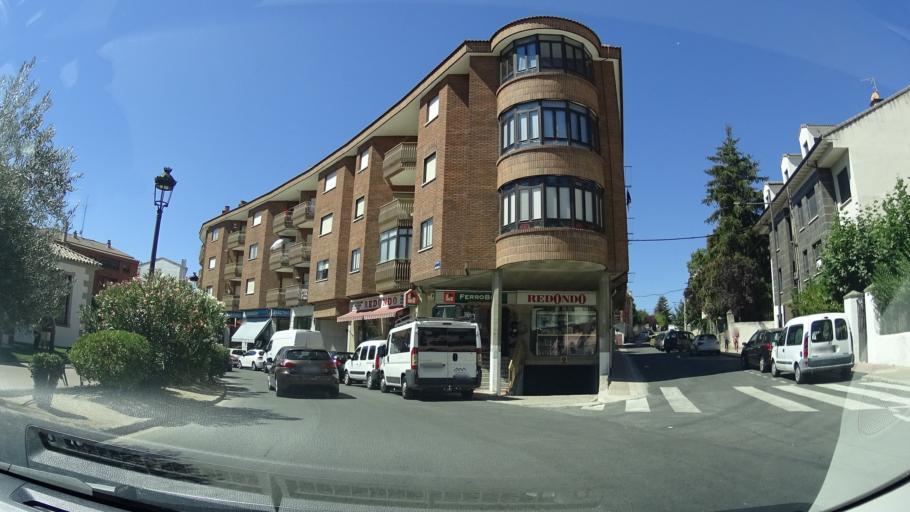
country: ES
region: Castille and Leon
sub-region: Provincia de Avila
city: Las Navas del Marques
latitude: 40.6030
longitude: -4.3346
